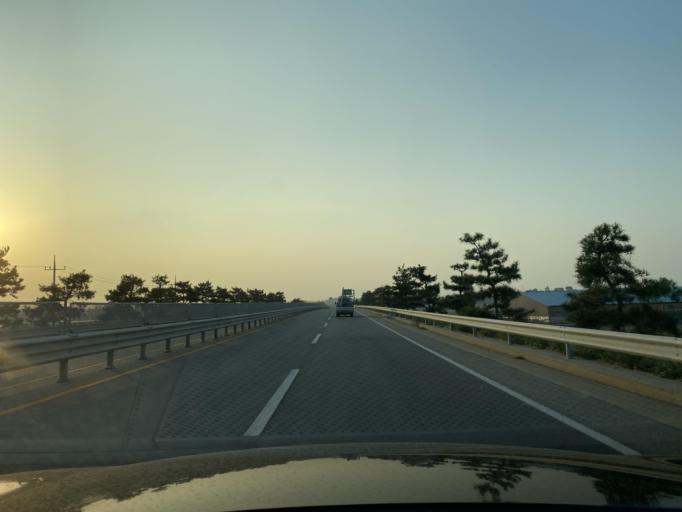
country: KR
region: Chungcheongnam-do
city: Yesan
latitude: 36.6969
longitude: 126.8055
